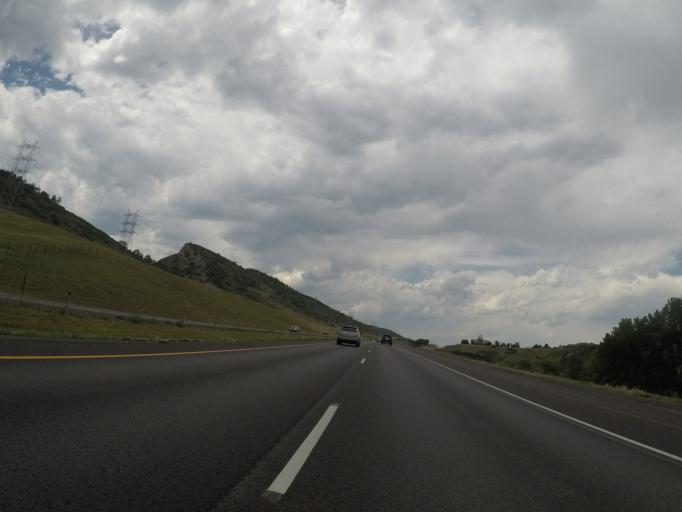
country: US
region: Colorado
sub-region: Jefferson County
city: Ken Caryl
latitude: 39.5984
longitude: -105.1514
